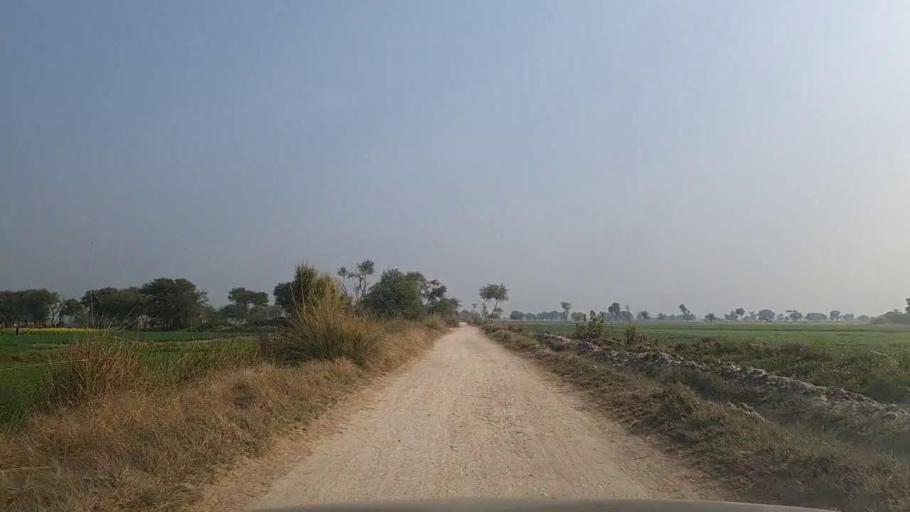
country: PK
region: Sindh
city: Nawabshah
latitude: 26.2888
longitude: 68.4438
